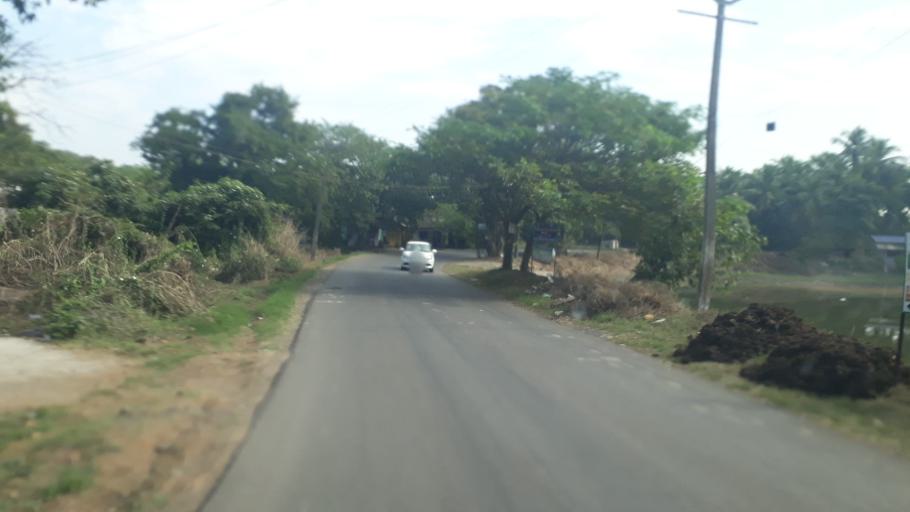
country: IN
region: Maharashtra
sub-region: Raigarh
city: Revadanda
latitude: 18.5948
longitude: 72.9220
